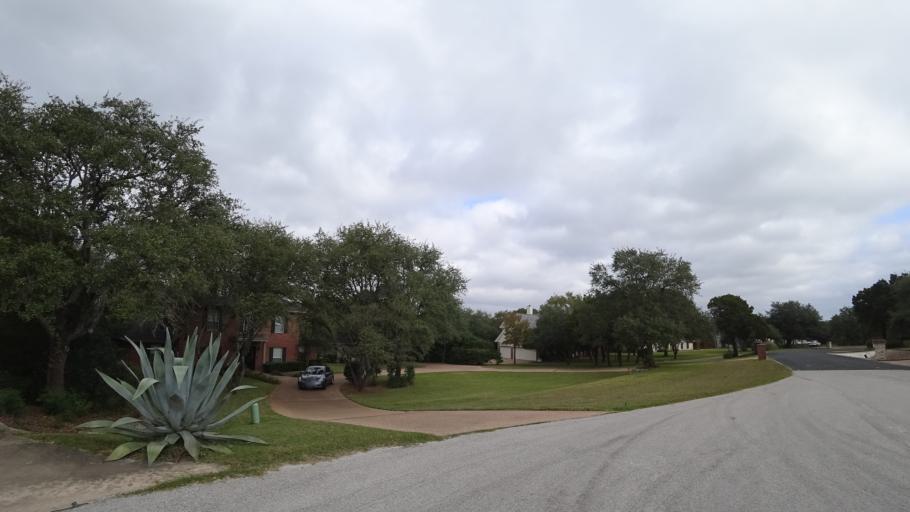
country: US
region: Texas
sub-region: Travis County
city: Barton Creek
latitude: 30.2521
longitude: -97.9112
